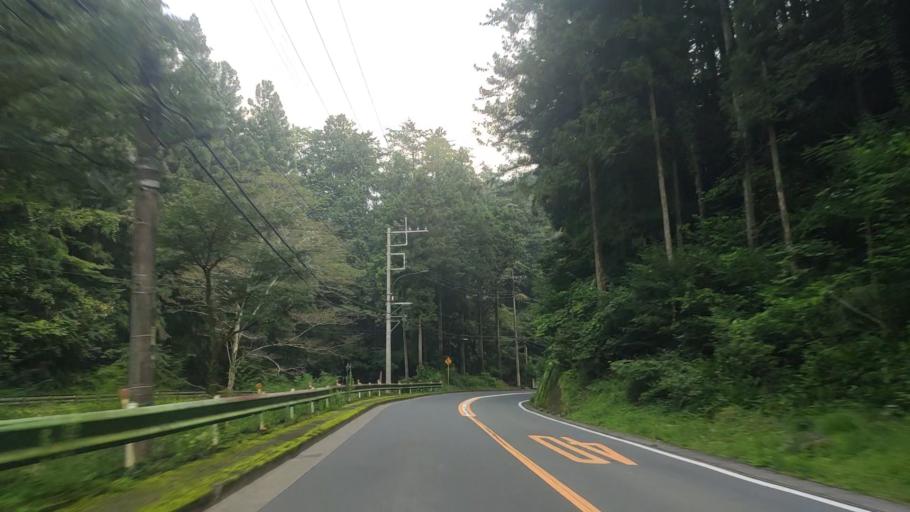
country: JP
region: Tokyo
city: Ome
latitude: 35.8379
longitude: 139.2165
